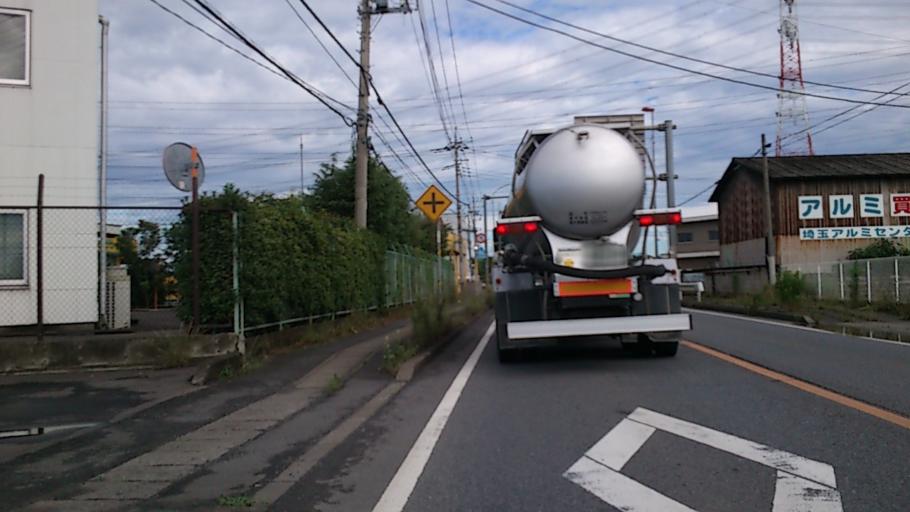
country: JP
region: Saitama
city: Honjo
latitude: 36.2247
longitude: 139.2234
